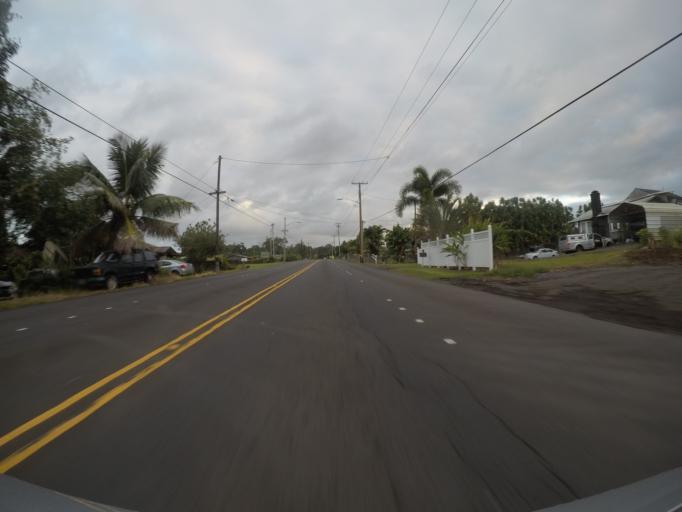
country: US
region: Hawaii
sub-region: Hawaii County
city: Hilo
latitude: 19.6781
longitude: -155.0670
